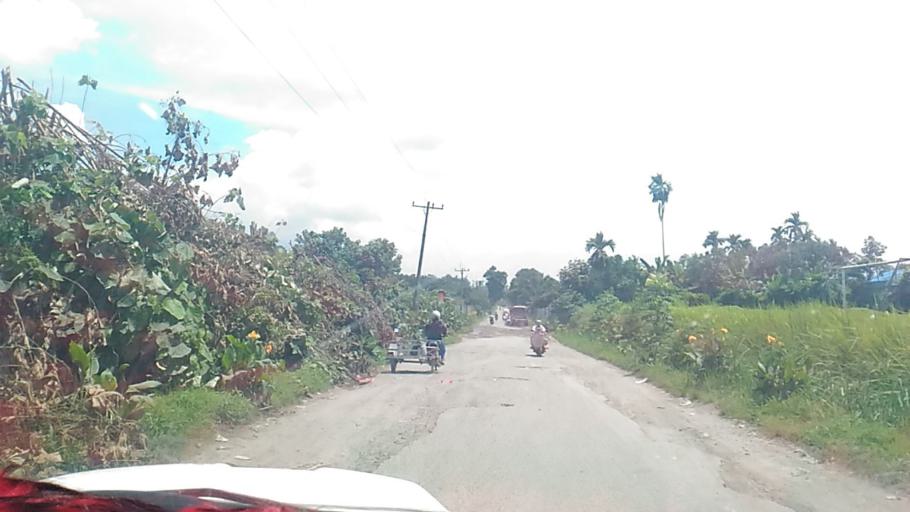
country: ID
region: North Sumatra
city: Sunggal
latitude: 3.5087
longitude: 98.5522
